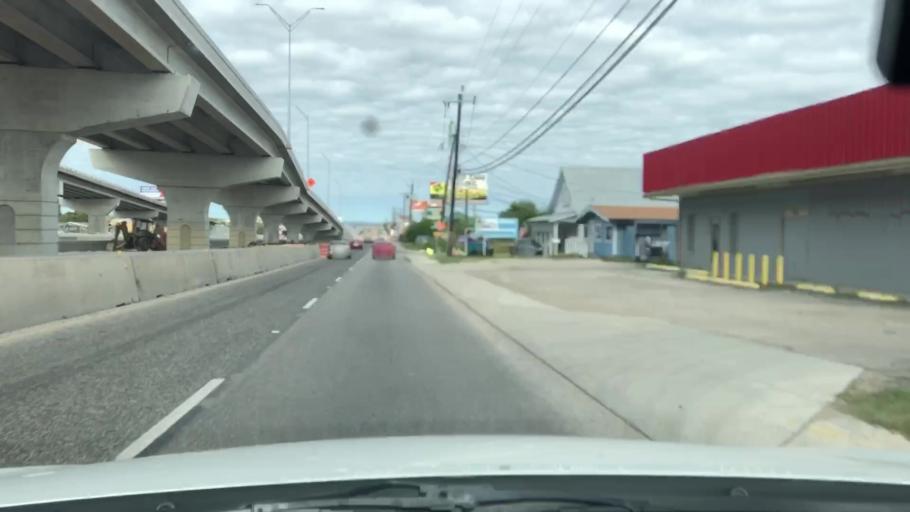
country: US
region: Texas
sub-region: Bexar County
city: Lackland Air Force Base
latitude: 29.4008
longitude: -98.6493
